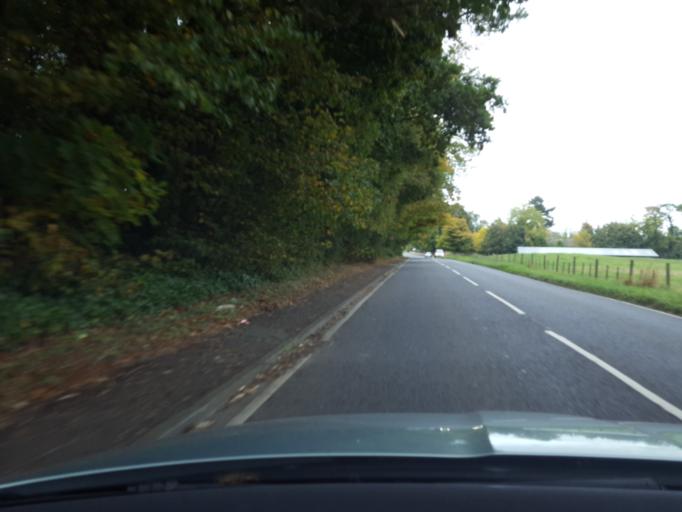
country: GB
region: Scotland
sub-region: Fife
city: Pathhead
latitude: 55.8691
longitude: -2.9914
